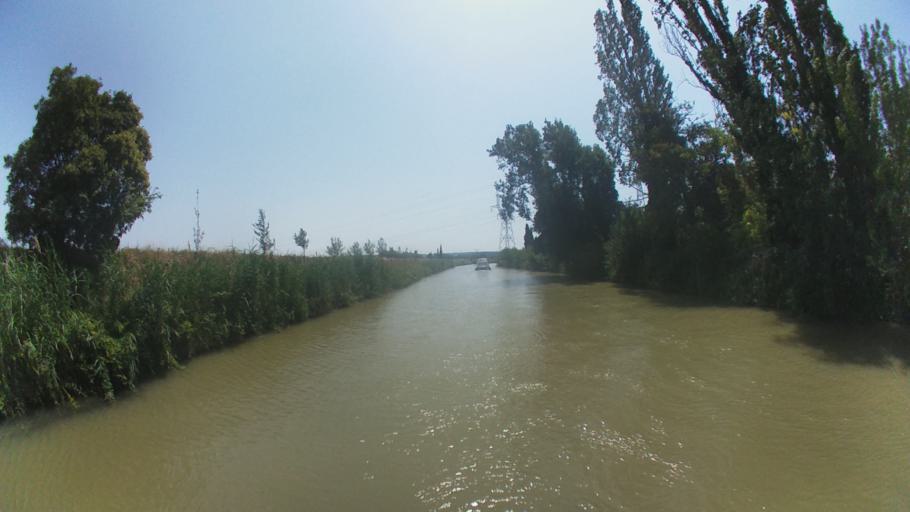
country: FR
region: Languedoc-Roussillon
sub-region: Departement de l'Aude
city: Azille
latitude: 43.2464
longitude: 2.6603
